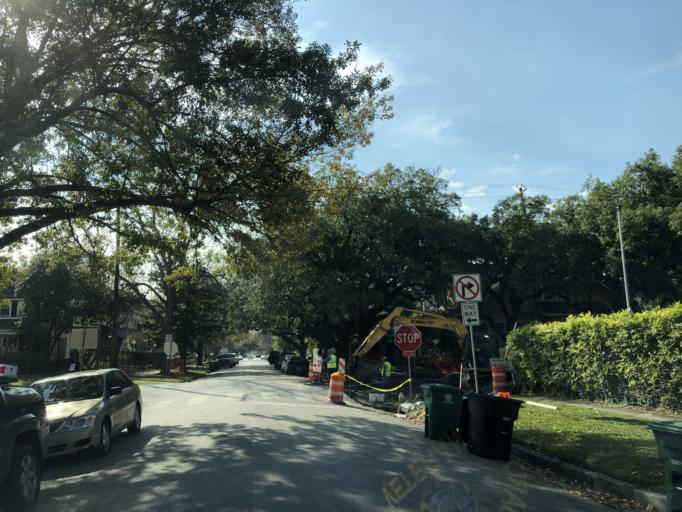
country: US
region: Texas
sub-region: Harris County
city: Houston
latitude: 29.7892
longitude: -95.3964
